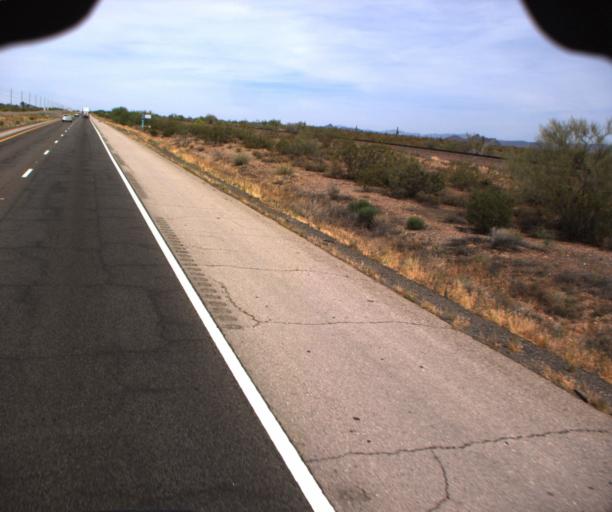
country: US
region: Arizona
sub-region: Maricopa County
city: Wickenburg
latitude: 33.8041
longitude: -112.5621
